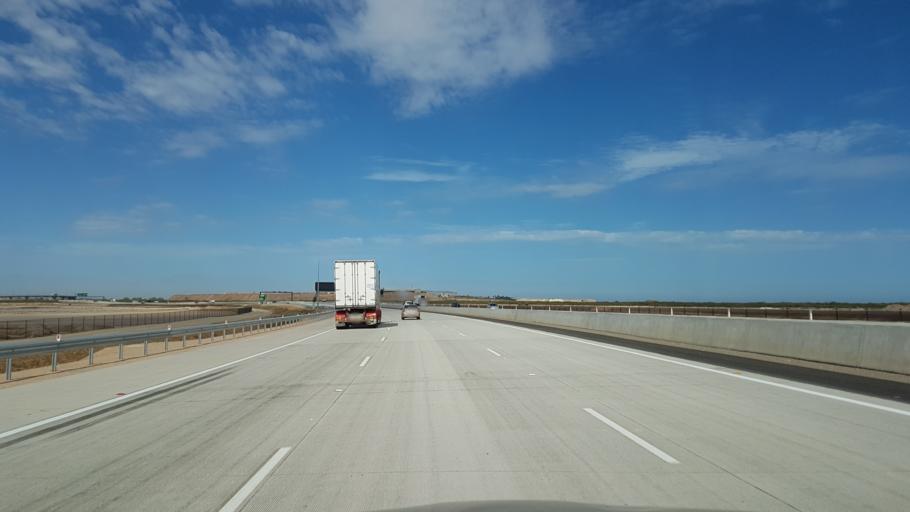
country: AU
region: South Australia
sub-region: Port Adelaide Enfield
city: Enfield
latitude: -34.8128
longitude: 138.5635
